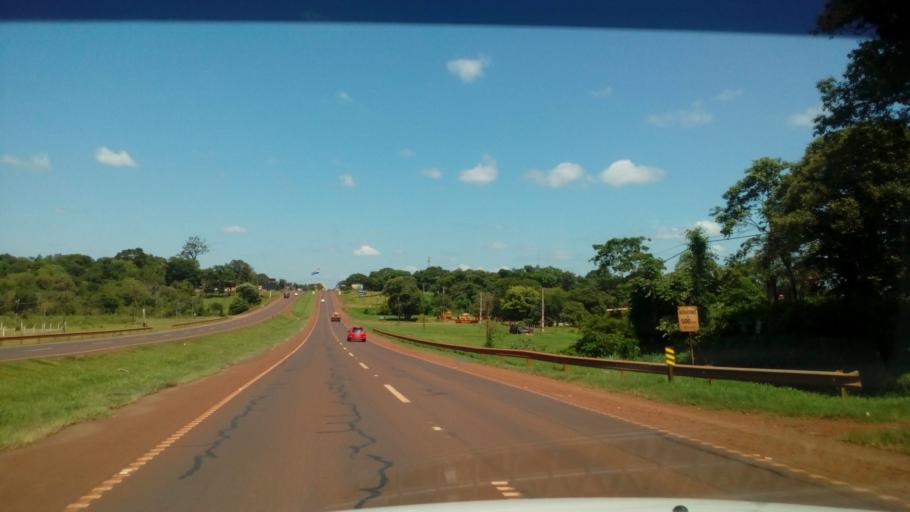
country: PY
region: Alto Parana
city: Colonia Yguazu
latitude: -25.4851
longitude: -54.8896
